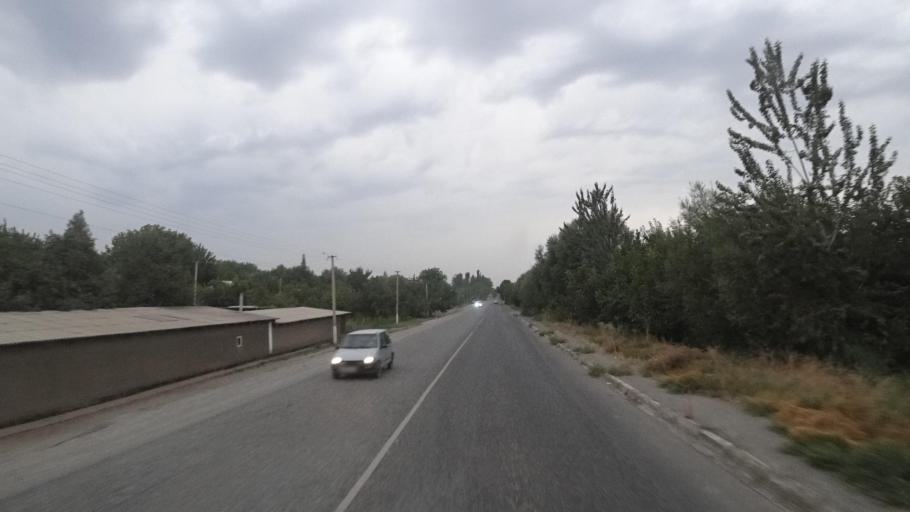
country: UZ
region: Namangan
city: Haqqulobod Shahri
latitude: 41.0494
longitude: 72.2913
